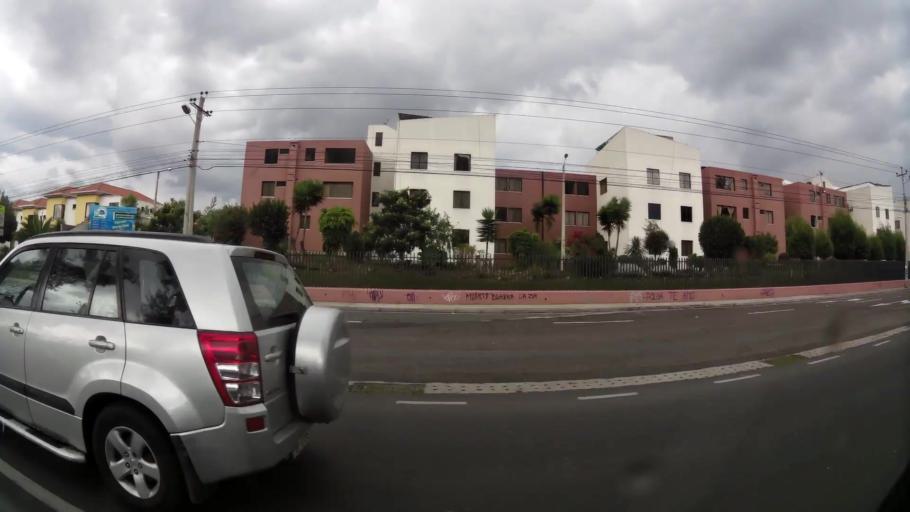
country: EC
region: Pichincha
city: Quito
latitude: -0.0684
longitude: -78.4685
